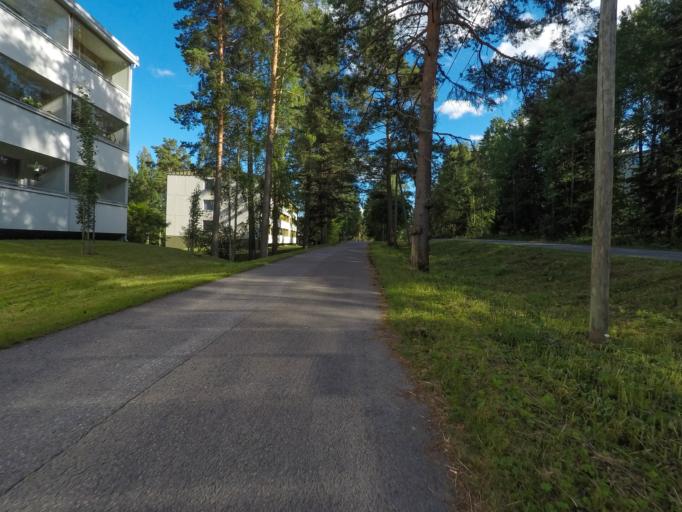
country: FI
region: South Karelia
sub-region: Lappeenranta
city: Lappeenranta
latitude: 61.0831
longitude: 28.1480
